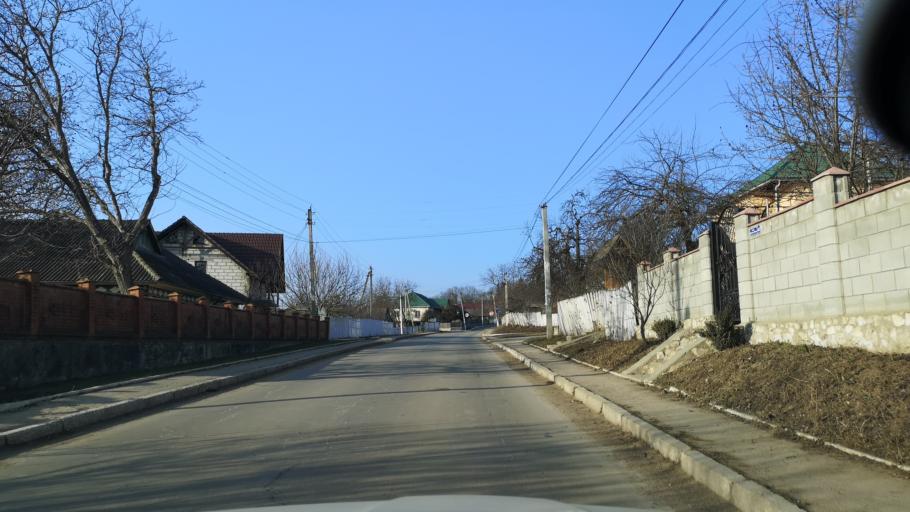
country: MD
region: Stinga Nistrului
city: Bucovat
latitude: 47.1145
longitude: 28.5075
